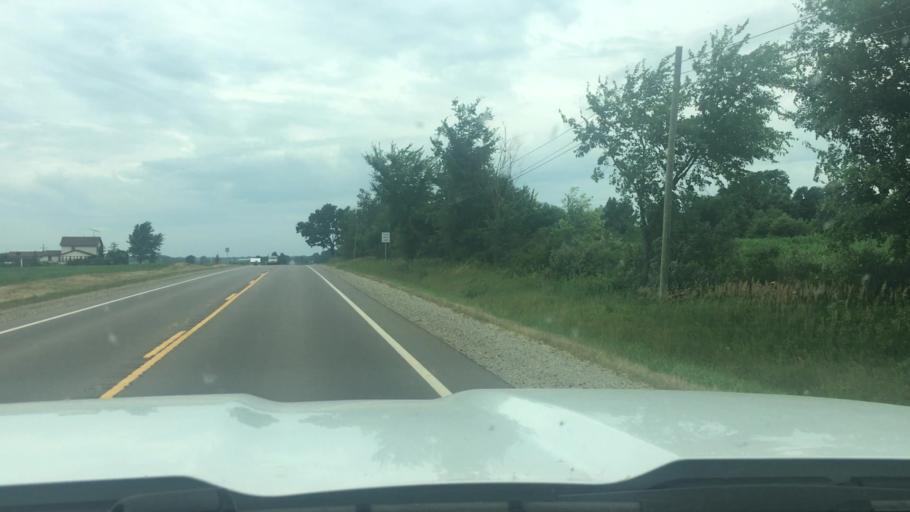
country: US
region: Michigan
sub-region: Clinton County
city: Fowler
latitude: 43.0019
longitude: -84.7718
